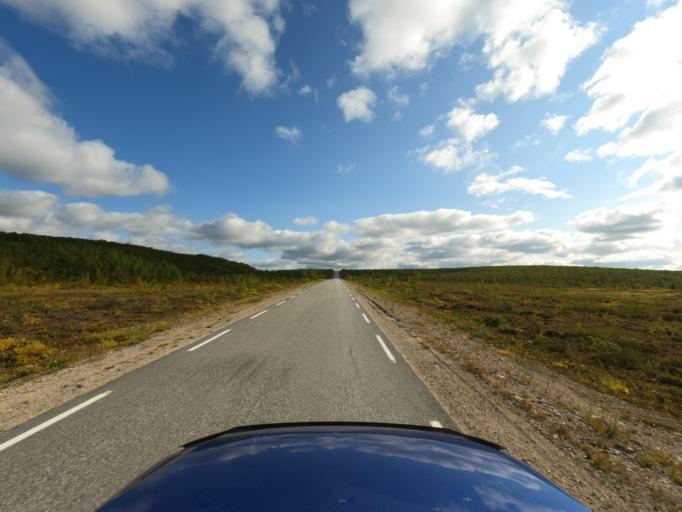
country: NO
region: Finnmark Fylke
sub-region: Porsanger
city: Lakselv
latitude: 69.3907
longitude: 24.5052
